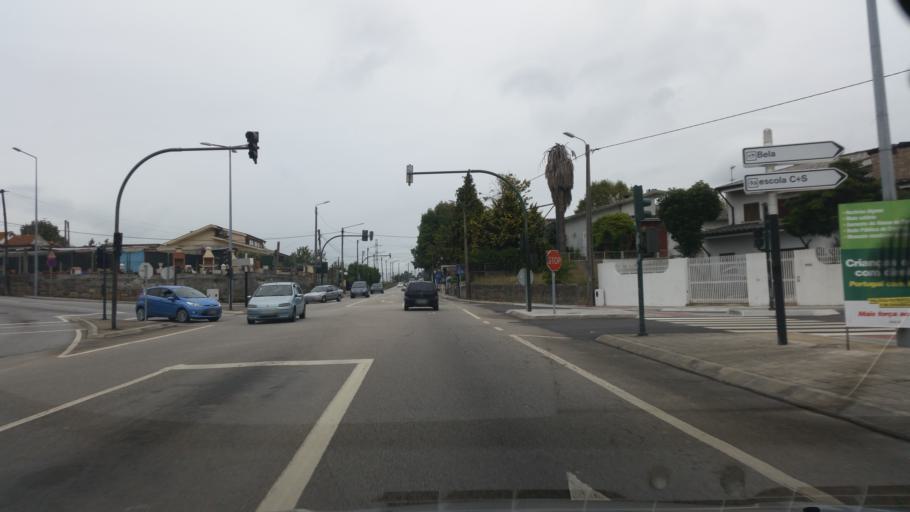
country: PT
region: Porto
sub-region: Valongo
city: Ermesinde
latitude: 41.2281
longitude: -8.5540
